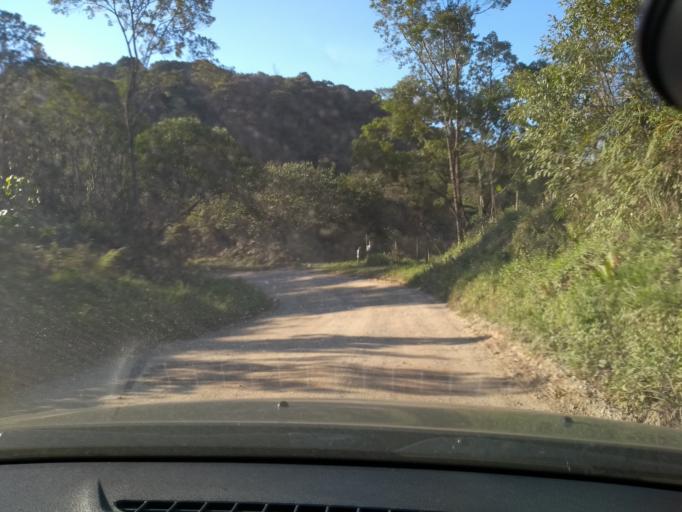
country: BR
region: Sao Paulo
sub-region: Rio Grande Da Serra
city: Rio Grande da Serra
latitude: -23.7753
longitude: -46.4980
